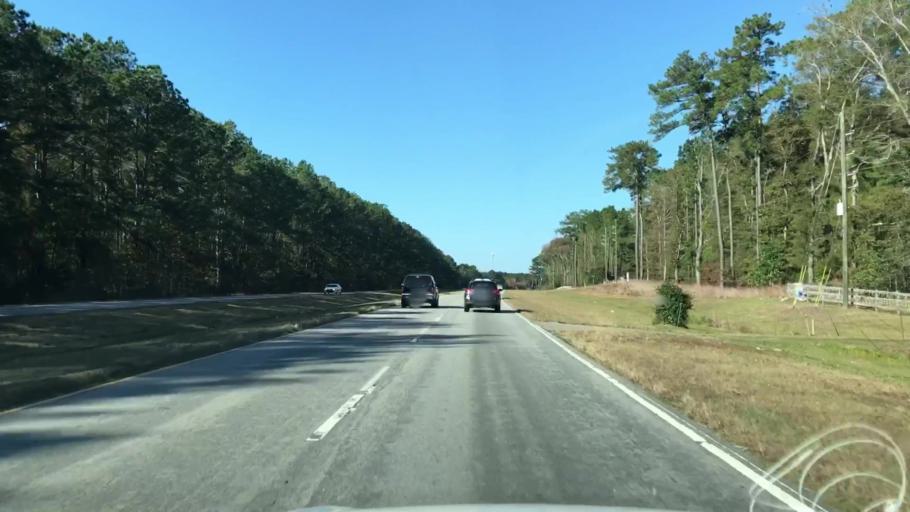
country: US
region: South Carolina
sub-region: Charleston County
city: Ravenel
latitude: 32.7574
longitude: -80.3750
